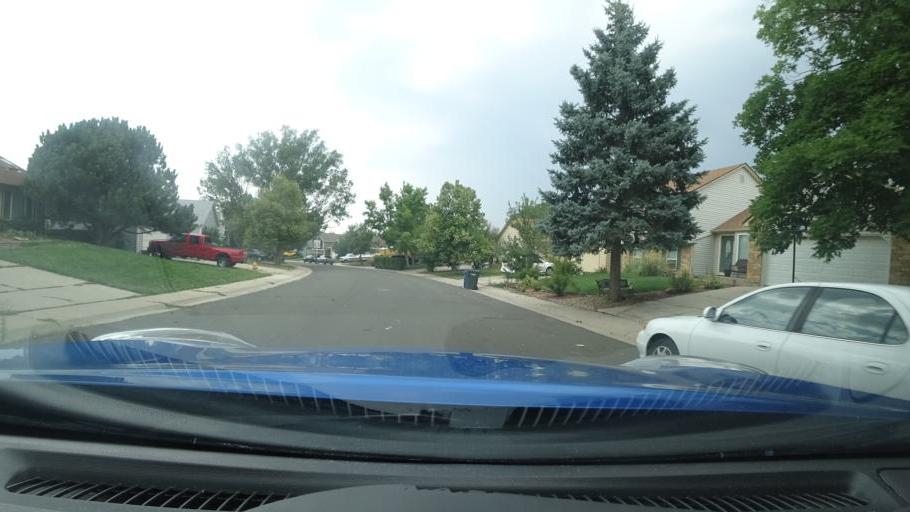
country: US
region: Colorado
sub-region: Adams County
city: Aurora
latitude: 39.6859
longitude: -104.7604
